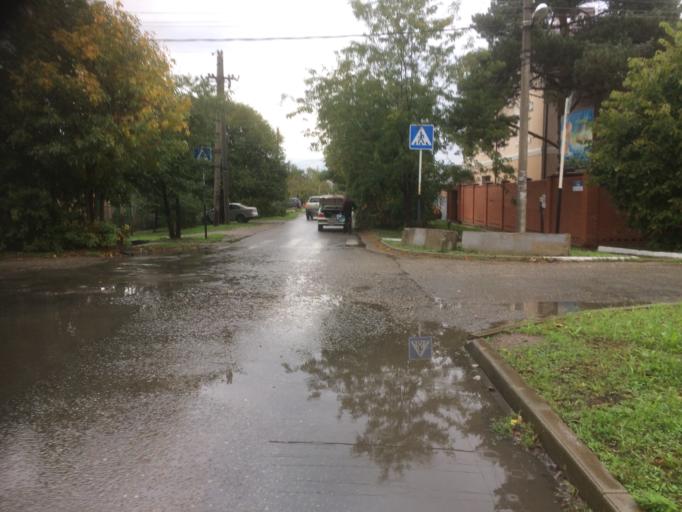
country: RU
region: Krasnodarskiy
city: Krasnodar
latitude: 45.0411
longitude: 38.9382
